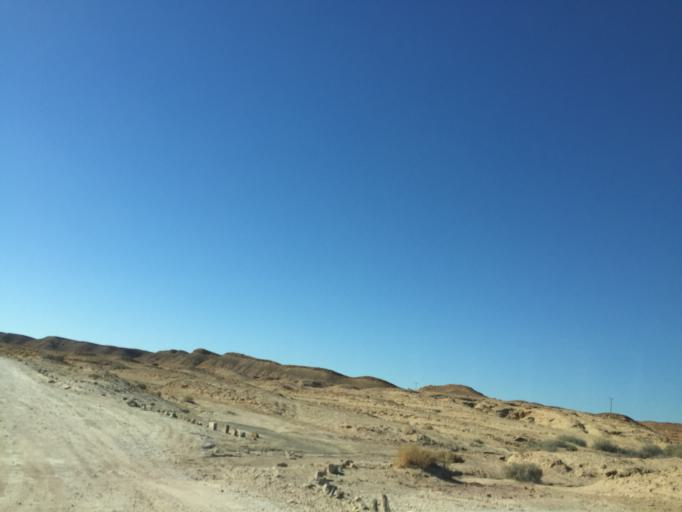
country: IL
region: Southern District
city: Mitzpe Ramon
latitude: 30.6148
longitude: 34.9061
